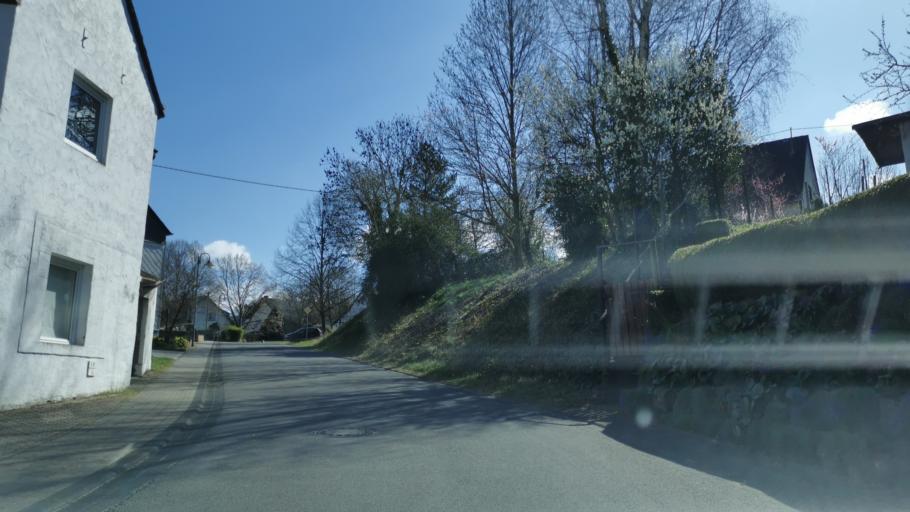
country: DE
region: Rheinland-Pfalz
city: Brauneberg
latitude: 49.9097
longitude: 6.9918
